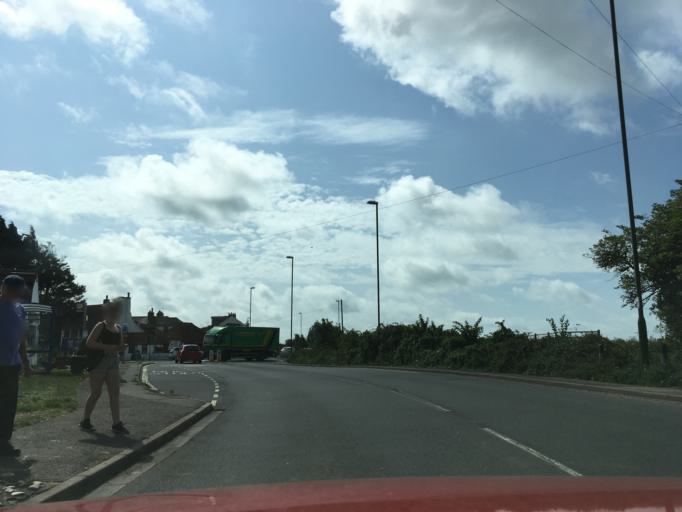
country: GB
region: England
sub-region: West Sussex
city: Shoreham-by-Sea
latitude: 50.8404
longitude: -0.2863
